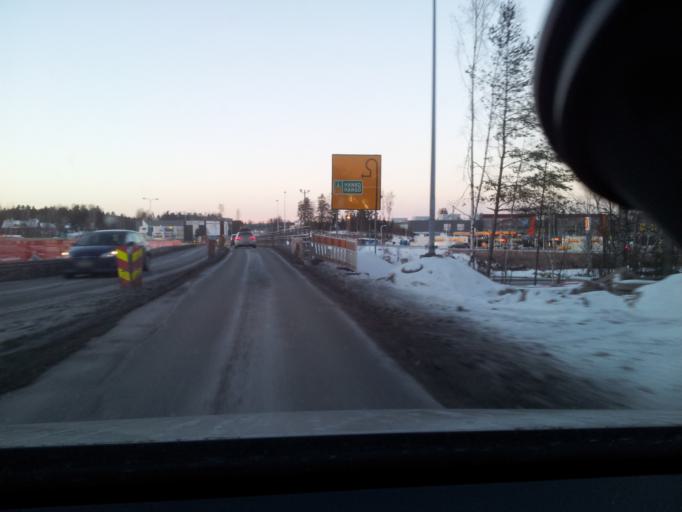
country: FI
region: Uusimaa
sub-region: Helsinki
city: Kauniainen
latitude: 60.1597
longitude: 24.7058
